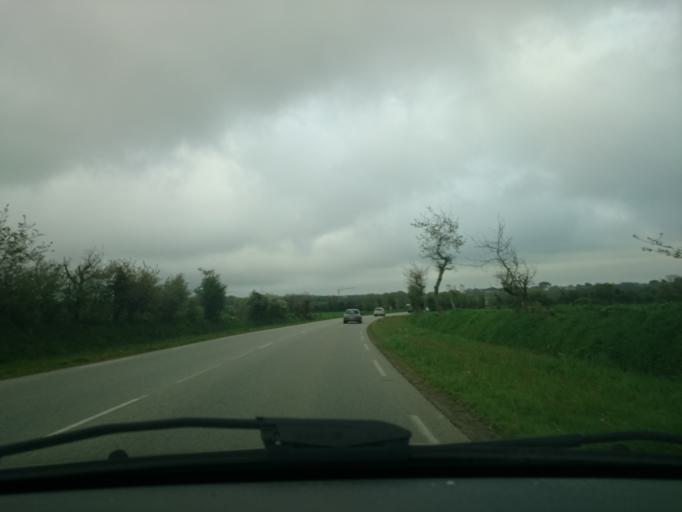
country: FR
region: Brittany
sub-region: Departement du Finistere
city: Saint-Renan
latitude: 48.4313
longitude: -4.6053
